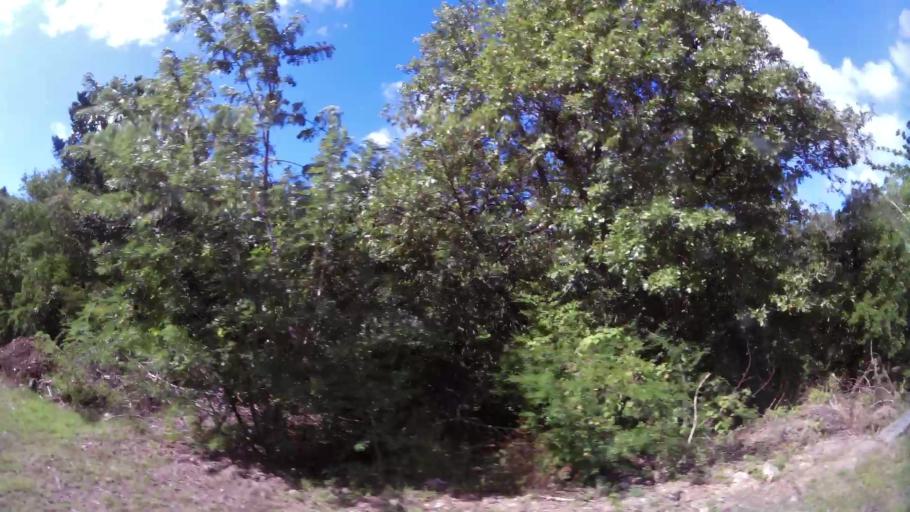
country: DM
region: Saint John
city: Portsmouth
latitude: 15.5888
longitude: -61.4639
